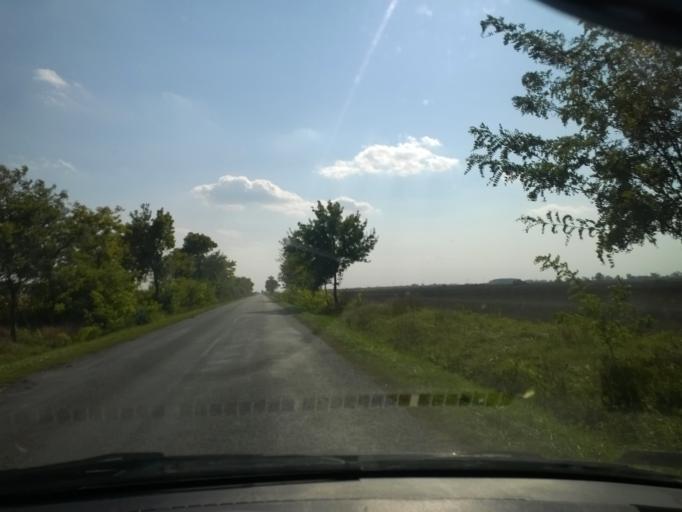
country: HU
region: Bacs-Kiskun
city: Kalocsa
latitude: 46.4978
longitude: 19.0526
